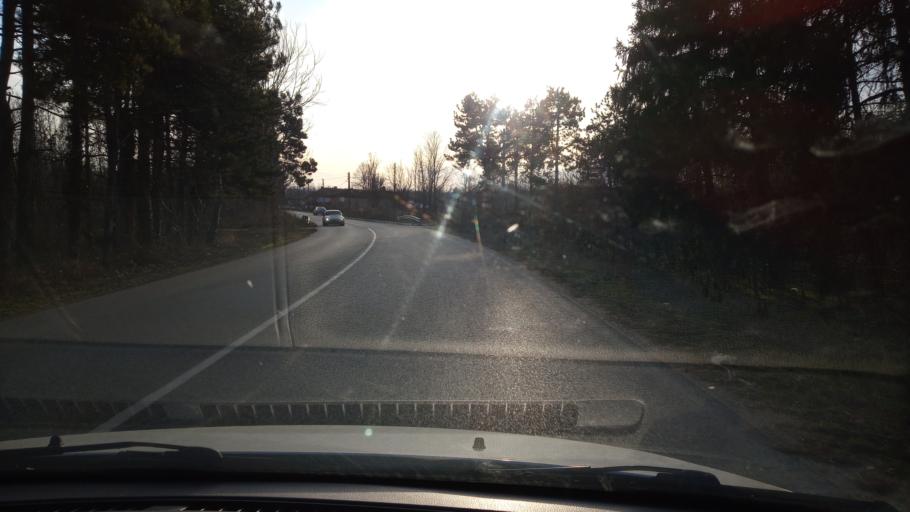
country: BG
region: Pleven
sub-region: Obshtina Pleven
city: Slavyanovo
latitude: 43.5623
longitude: 24.8700
